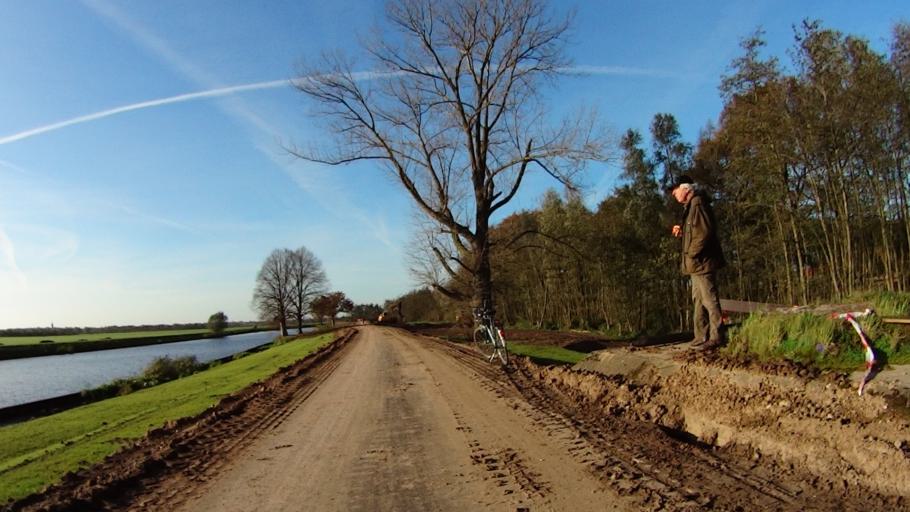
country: NL
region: Utrecht
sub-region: Gemeente Amersfoort
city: Hoogland
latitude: 52.1768
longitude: 5.3464
